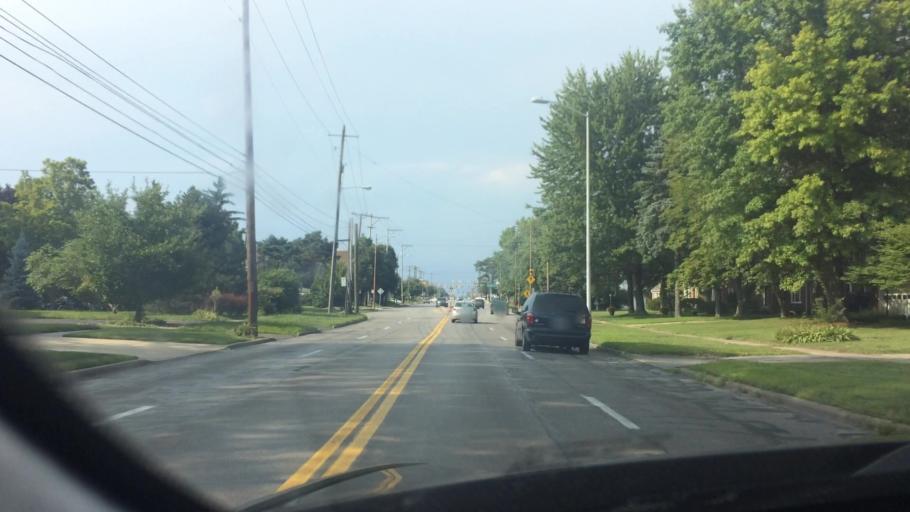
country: US
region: Ohio
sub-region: Lucas County
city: Ottawa Hills
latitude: 41.6738
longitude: -83.6225
